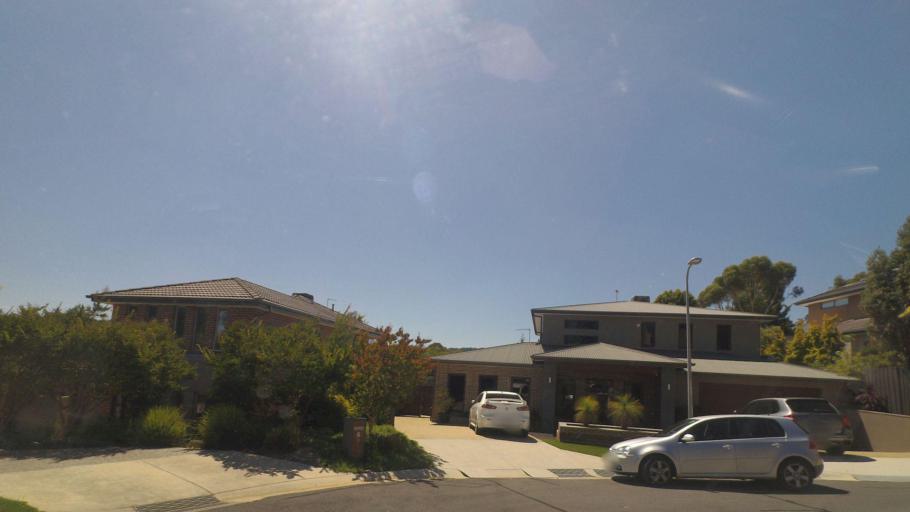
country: AU
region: Victoria
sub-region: Maroondah
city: Warranwood
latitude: -37.7814
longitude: 145.2390
